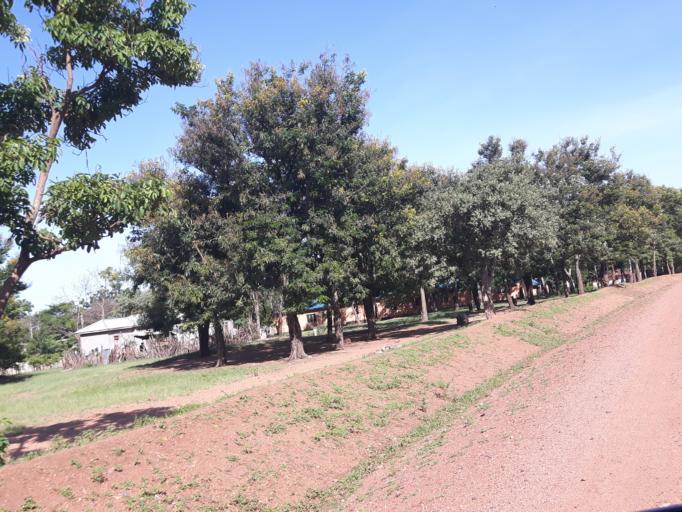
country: TZ
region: Mara
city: Issenye
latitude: -2.0247
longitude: 34.4507
